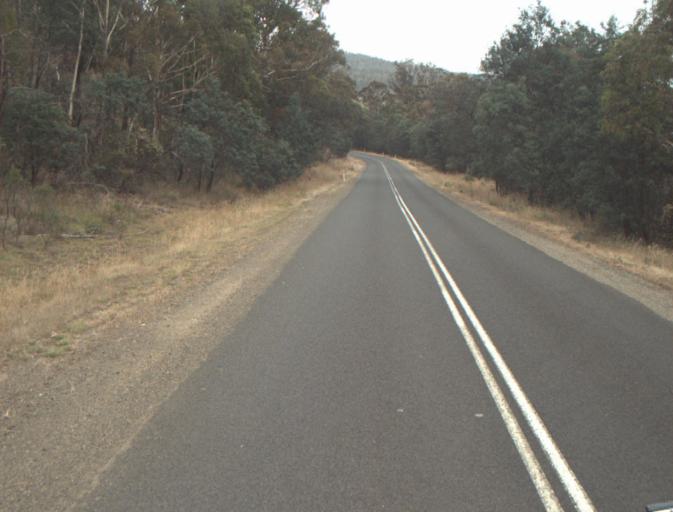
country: AU
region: Tasmania
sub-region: Northern Midlands
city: Evandale
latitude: -41.5032
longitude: 147.3805
